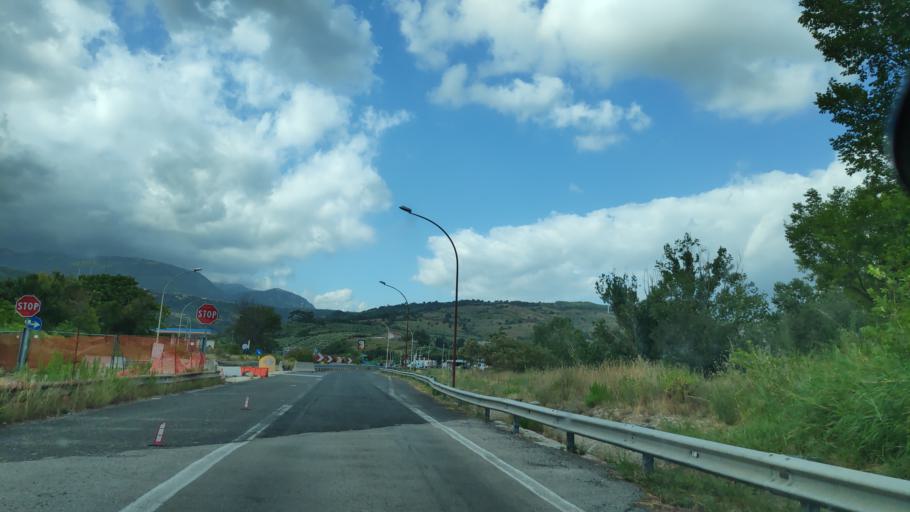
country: IT
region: Campania
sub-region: Provincia di Salerno
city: Serre
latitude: 40.6214
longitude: 15.1817
